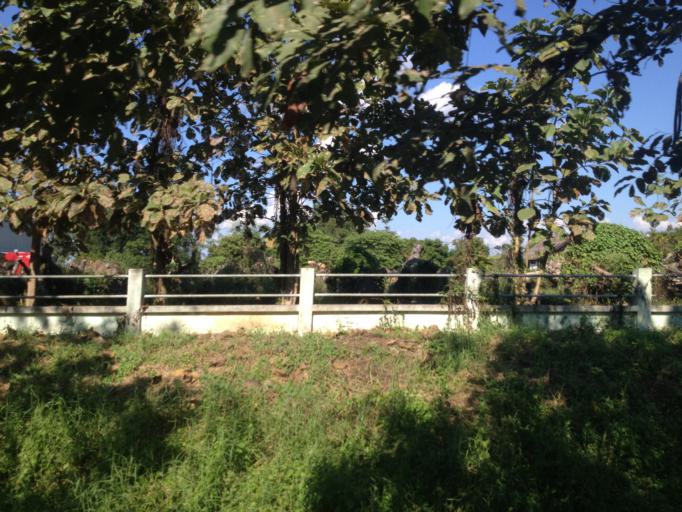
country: TH
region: Chiang Mai
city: Hang Dong
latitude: 18.6817
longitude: 98.9797
